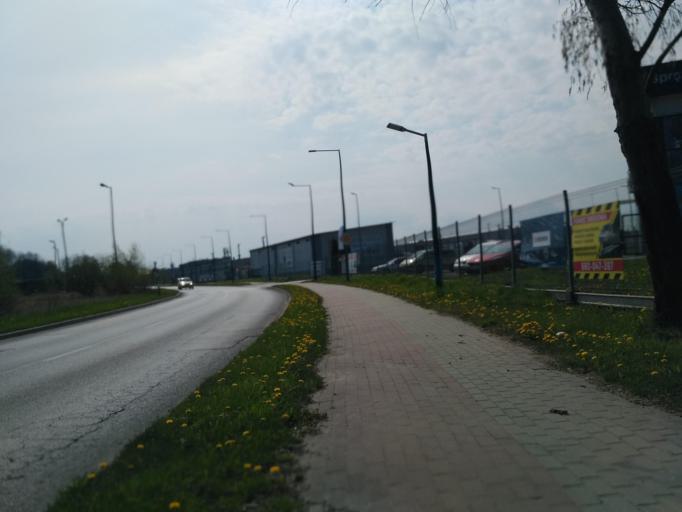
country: PL
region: Subcarpathian Voivodeship
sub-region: Krosno
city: Krosno
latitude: 49.6802
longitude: 21.7231
